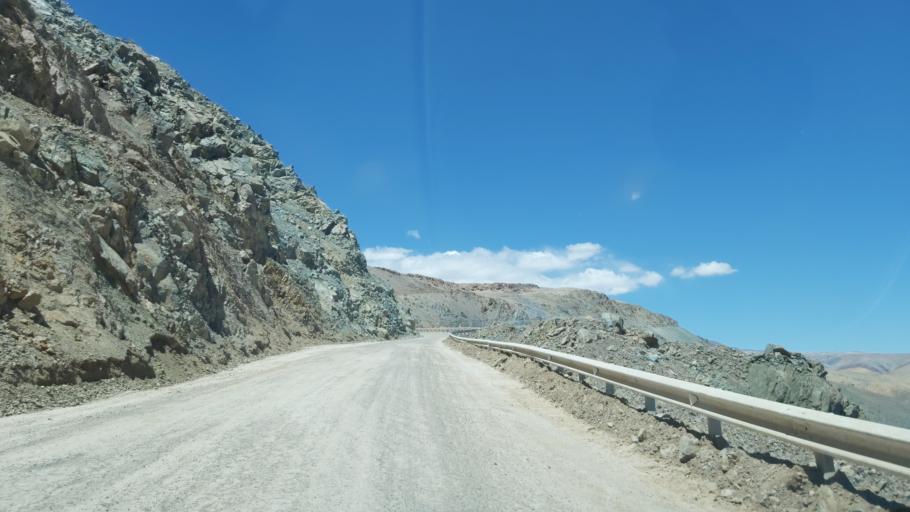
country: CL
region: Atacama
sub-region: Provincia de Chanaral
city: Diego de Almagro
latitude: -26.4593
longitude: -69.3099
